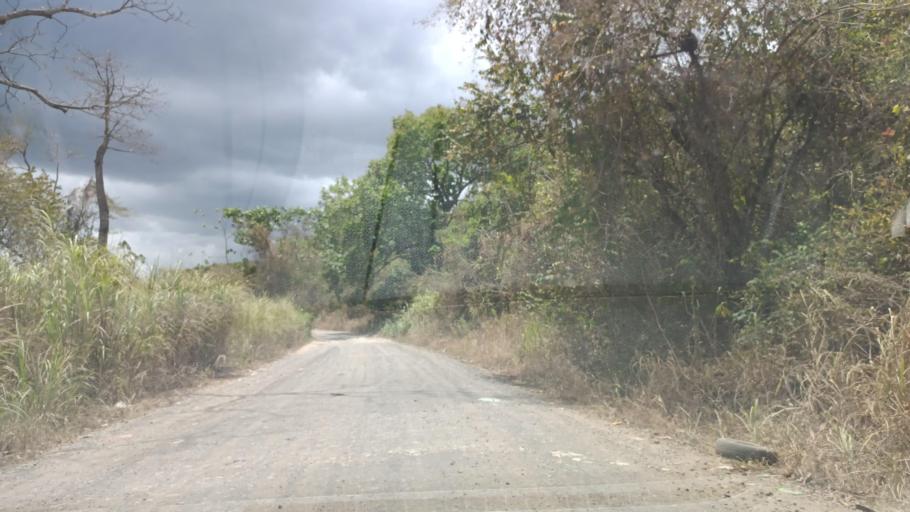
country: PA
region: Panama
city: Las Cumbres
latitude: 9.0594
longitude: -79.5673
